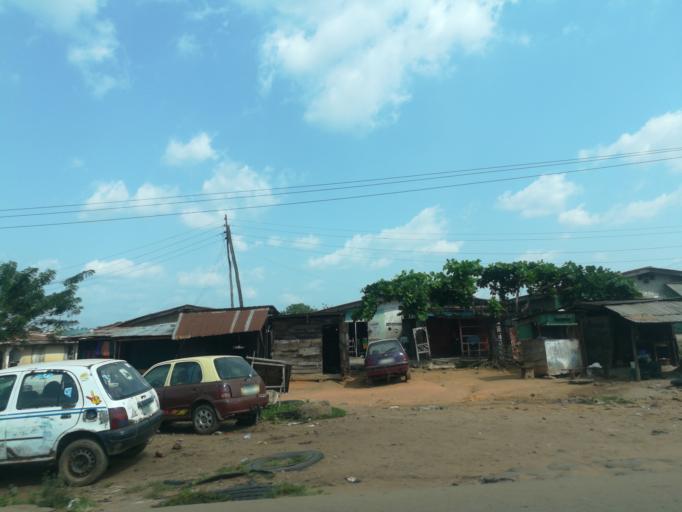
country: NG
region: Oyo
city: Moniya
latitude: 7.5324
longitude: 3.9114
